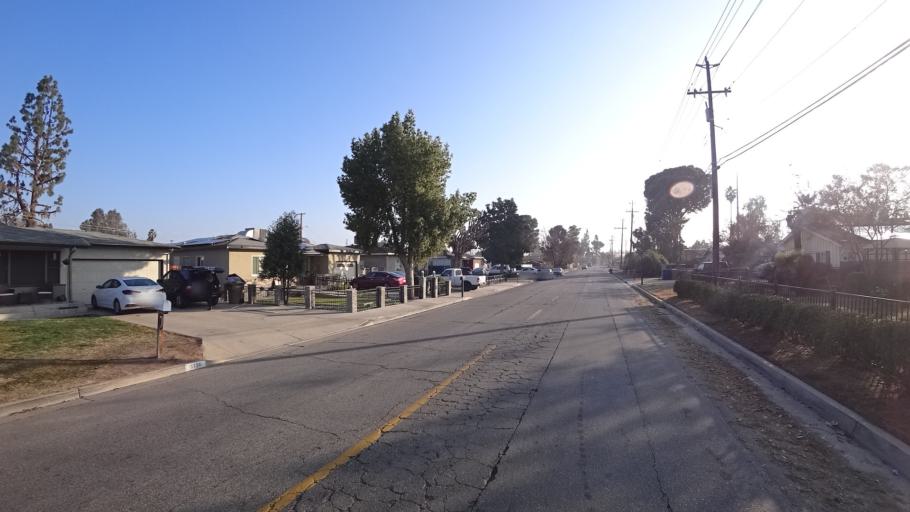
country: US
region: California
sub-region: Kern County
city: Bakersfield
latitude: 35.3625
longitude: -119.0458
